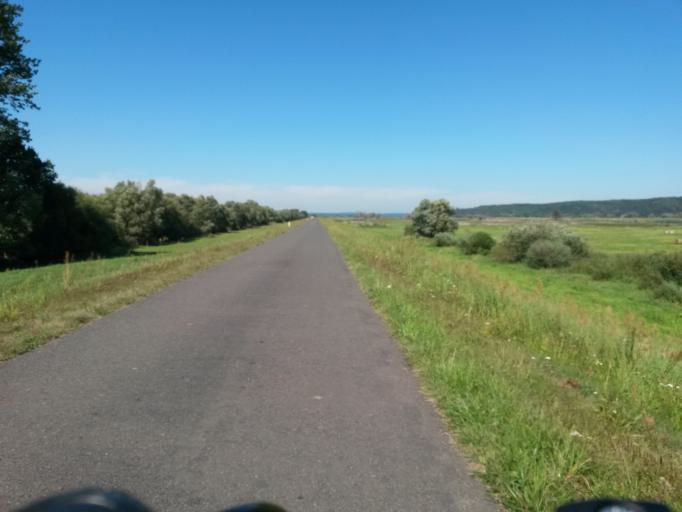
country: PL
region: West Pomeranian Voivodeship
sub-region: Powiat gryfinski
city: Cedynia
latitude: 52.9094
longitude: 14.1461
